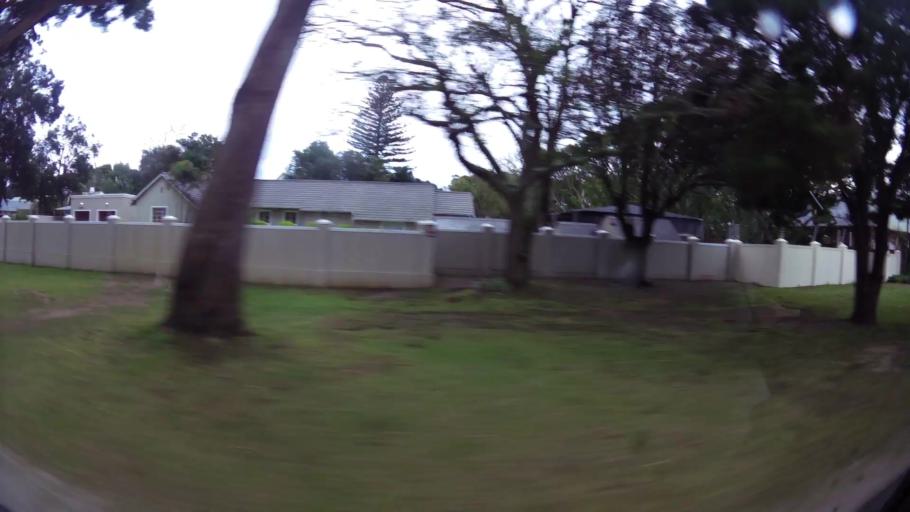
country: ZA
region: Eastern Cape
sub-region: Nelson Mandela Bay Metropolitan Municipality
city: Port Elizabeth
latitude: -33.9772
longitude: 25.5756
